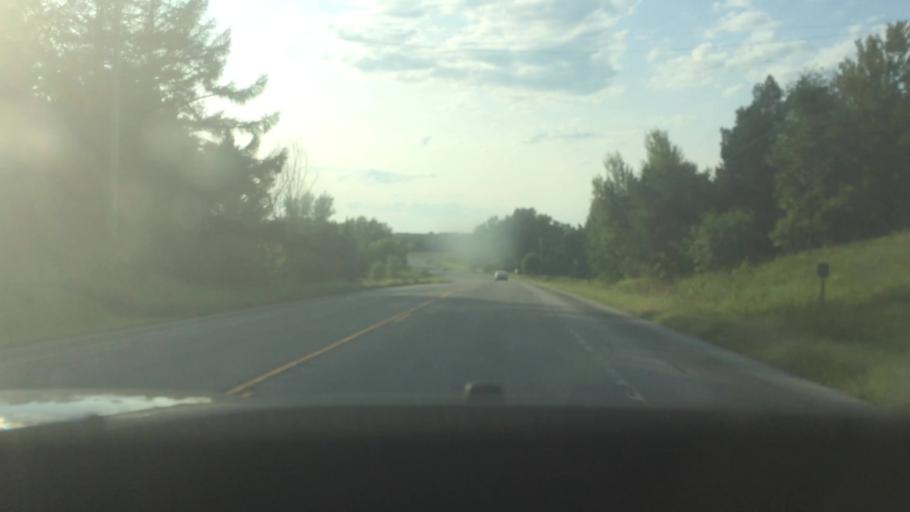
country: US
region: New York
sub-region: St. Lawrence County
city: Canton
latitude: 44.6060
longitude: -75.2064
